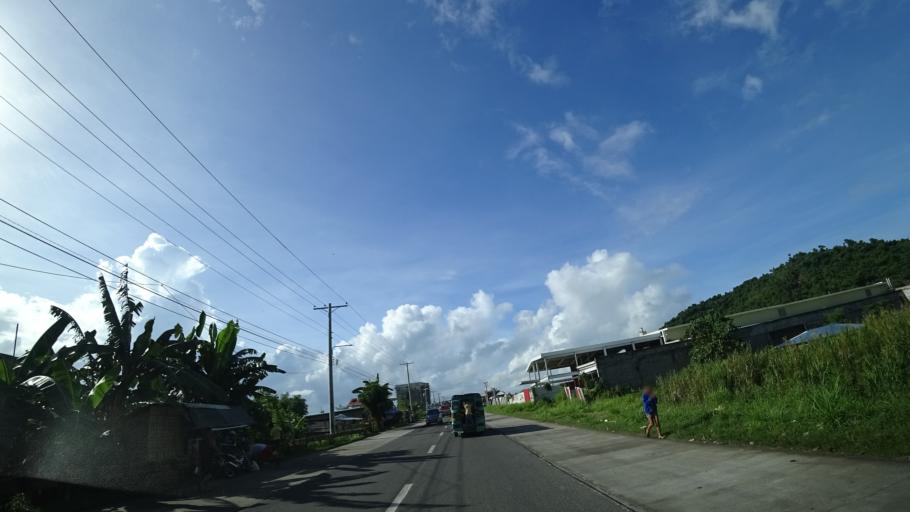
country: PH
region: Eastern Visayas
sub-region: Province of Leyte
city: Pawing
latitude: 11.1934
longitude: 124.9925
